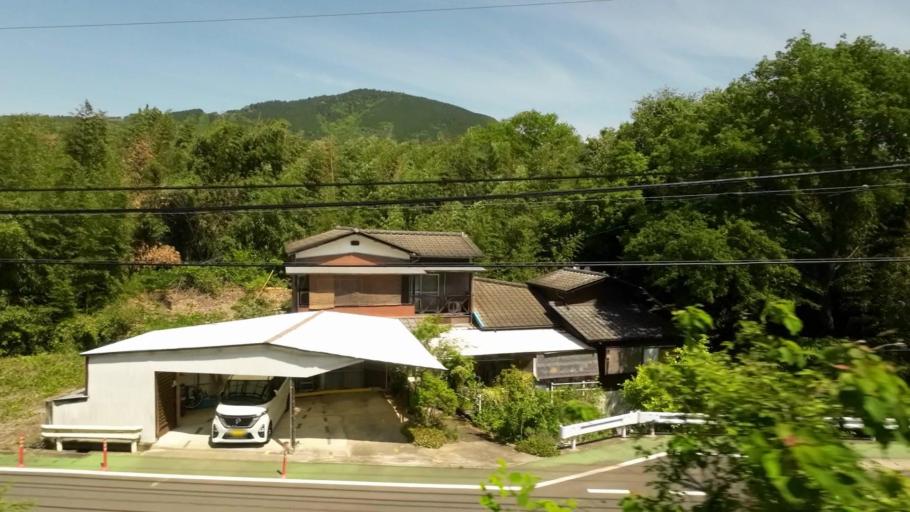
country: JP
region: Tokushima
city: Ikedacho
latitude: 34.0326
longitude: 133.8528
